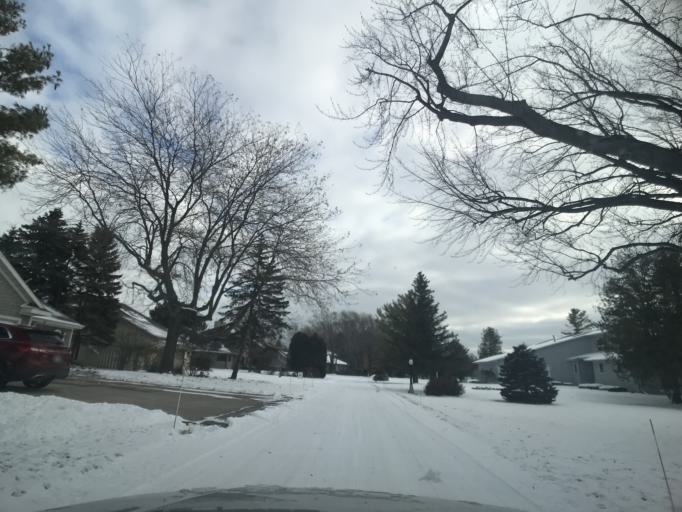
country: US
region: Wisconsin
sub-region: Door County
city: Sturgeon Bay
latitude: 44.8222
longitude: -87.3684
